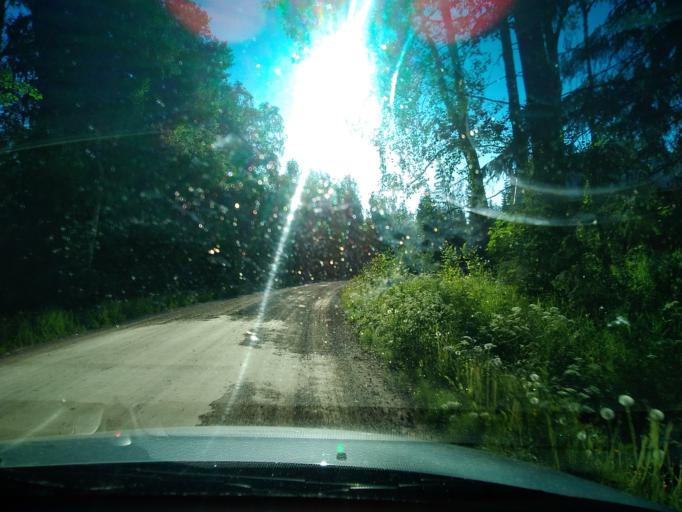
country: FI
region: Haeme
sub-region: Forssa
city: Tammela
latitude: 60.7475
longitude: 23.7246
